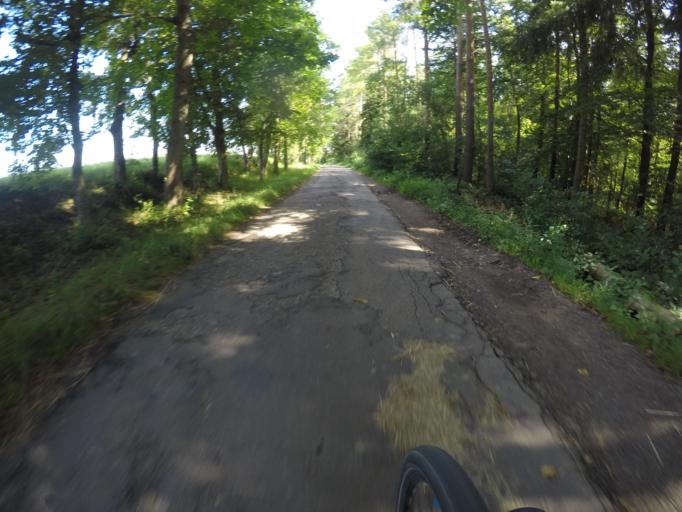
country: DE
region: Baden-Wuerttemberg
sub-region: Karlsruhe Region
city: Monsheim
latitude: 48.8811
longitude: 8.8756
